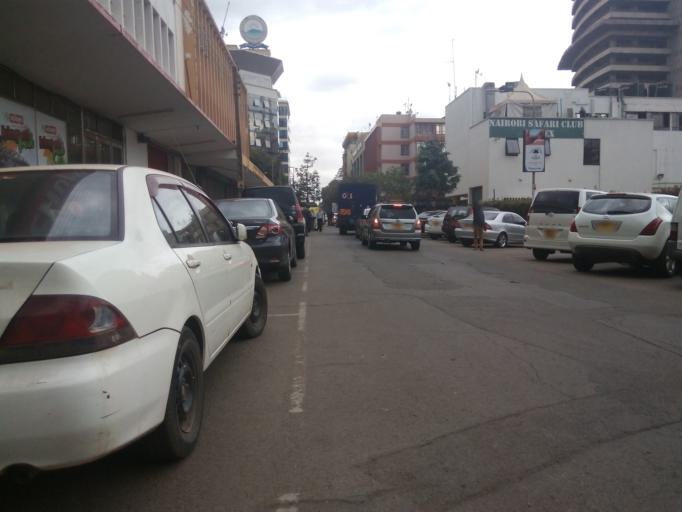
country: KE
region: Nairobi Area
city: Nairobi
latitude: -1.2820
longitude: 36.8169
